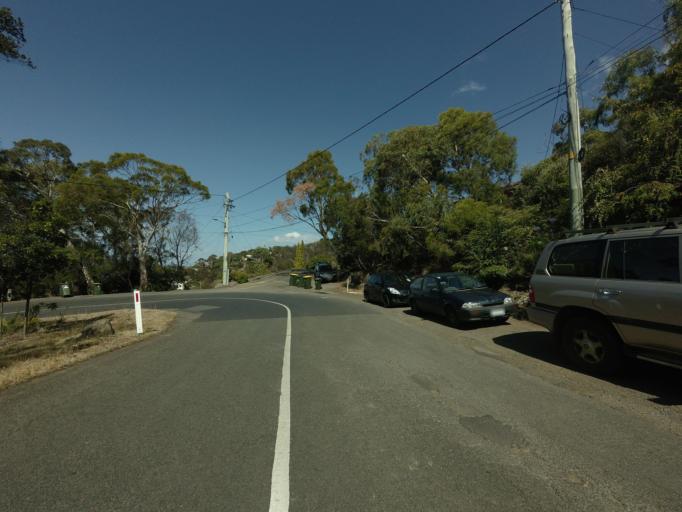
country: AU
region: Tasmania
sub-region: Hobart
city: Dynnyrne
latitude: -42.9134
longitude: 147.3273
